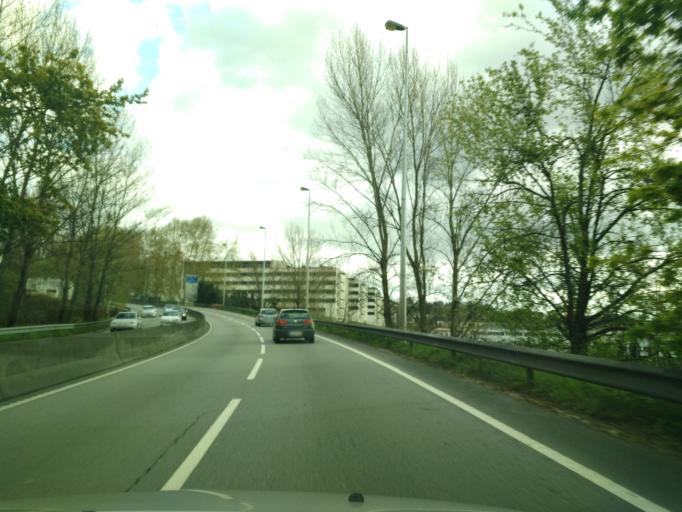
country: PT
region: Braga
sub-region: Guimaraes
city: Guimaraes
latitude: 41.4370
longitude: -8.3048
